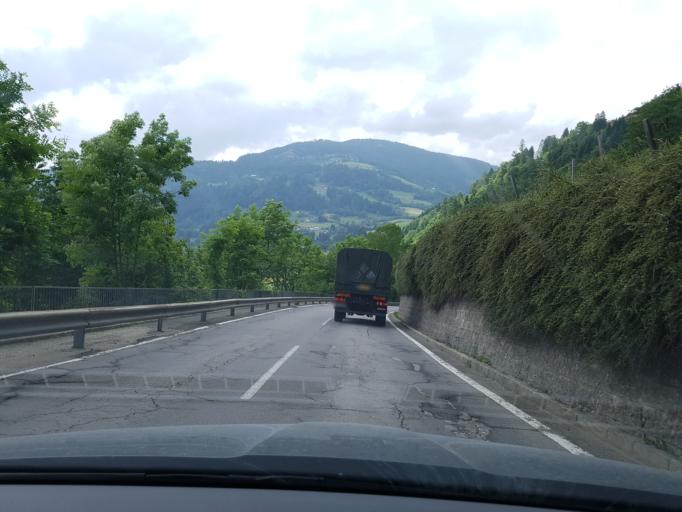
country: AT
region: Carinthia
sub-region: Politischer Bezirk Spittal an der Drau
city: Radenthein
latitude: 46.8000
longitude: 13.7196
